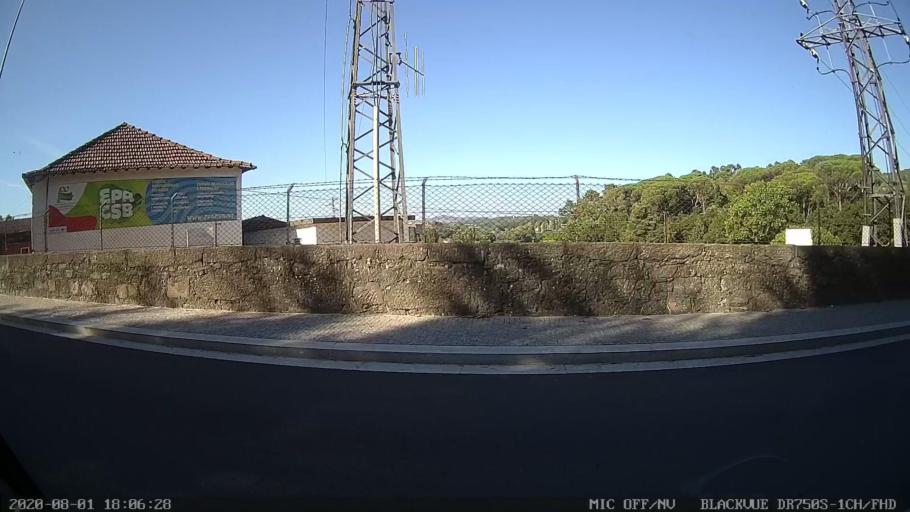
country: PT
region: Porto
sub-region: Santo Tirso
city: Santo Tirso
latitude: 41.3432
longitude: -8.4698
